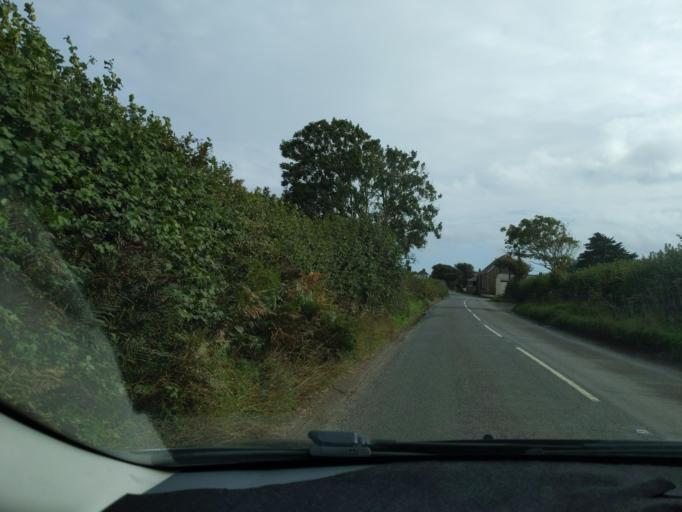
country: GB
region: England
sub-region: Cornwall
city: Mevagissey
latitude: 50.2549
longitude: -4.8247
